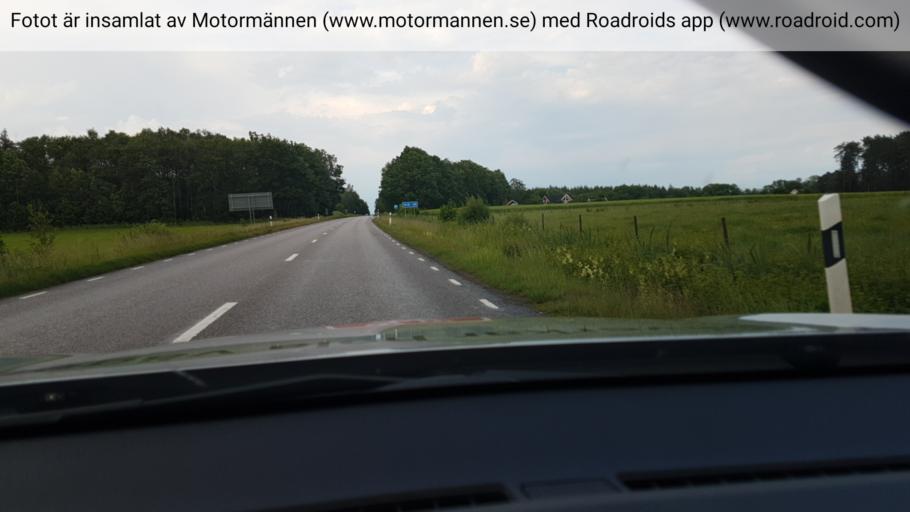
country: SE
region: Vaestra Goetaland
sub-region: Hjo Kommun
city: Hjo
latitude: 58.2284
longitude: 14.2141
